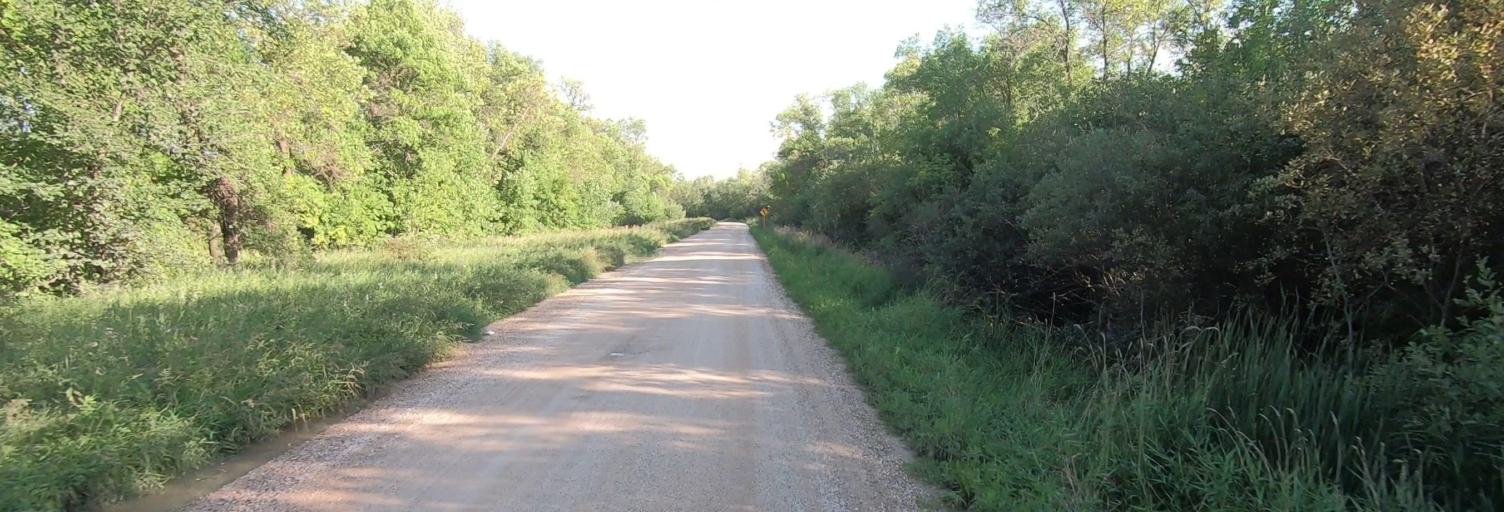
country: CA
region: Manitoba
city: Selkirk
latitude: 50.2876
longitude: -96.8646
